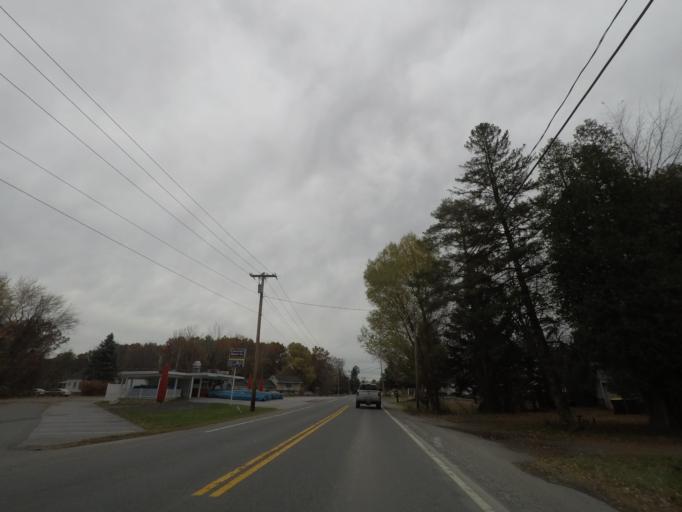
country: US
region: New York
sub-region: Albany County
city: Cohoes
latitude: 42.8205
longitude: -73.7513
